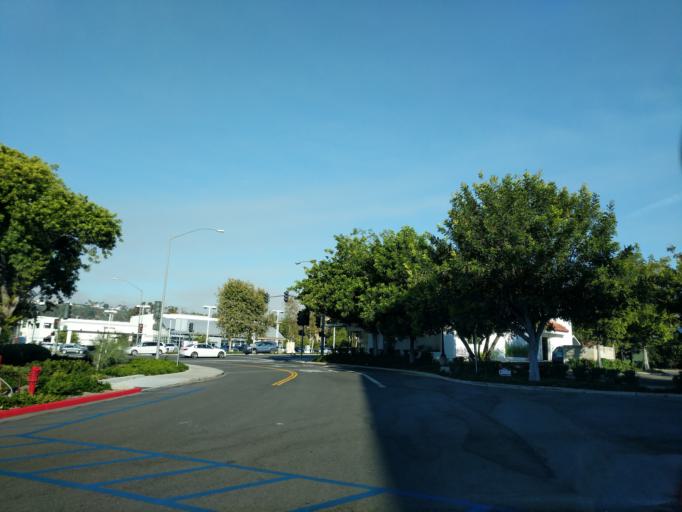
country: US
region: California
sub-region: Orange County
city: Ladera Ranch
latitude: 33.5497
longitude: -117.6700
